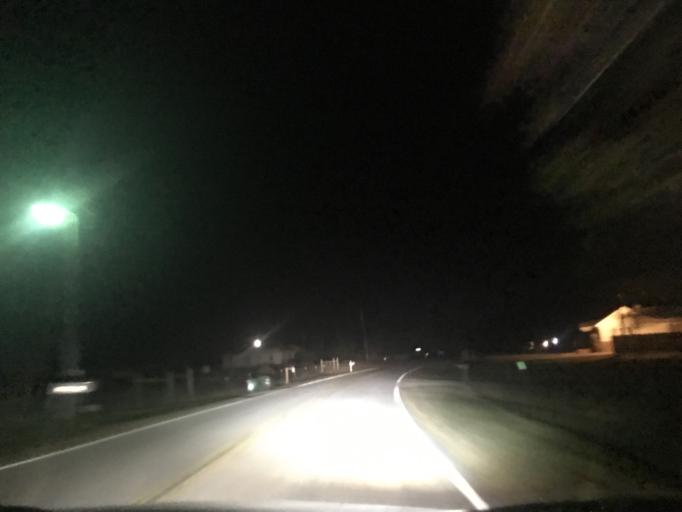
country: US
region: South Carolina
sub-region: Spartanburg County
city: Mayo
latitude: 35.1056
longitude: -81.8048
